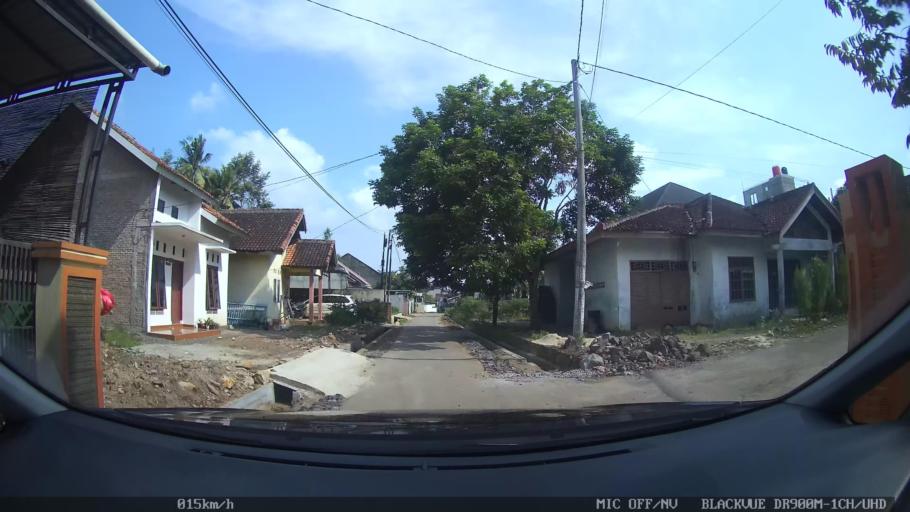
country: ID
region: Lampung
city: Kedaton
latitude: -5.3820
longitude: 105.2408
